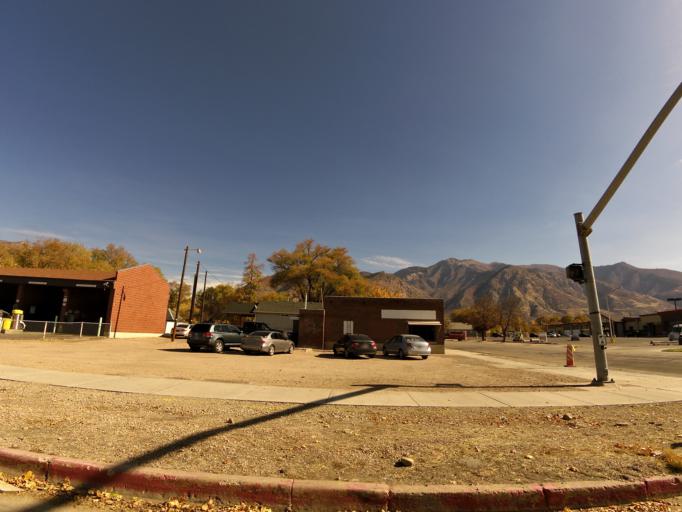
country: US
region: Utah
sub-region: Weber County
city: Ogden
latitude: 41.2227
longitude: -111.9592
